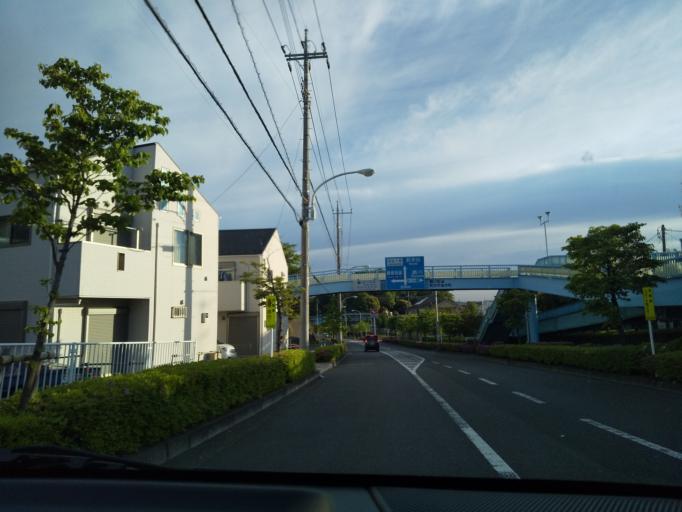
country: JP
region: Tokyo
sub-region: Machida-shi
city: Machida
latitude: 35.5695
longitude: 139.4543
